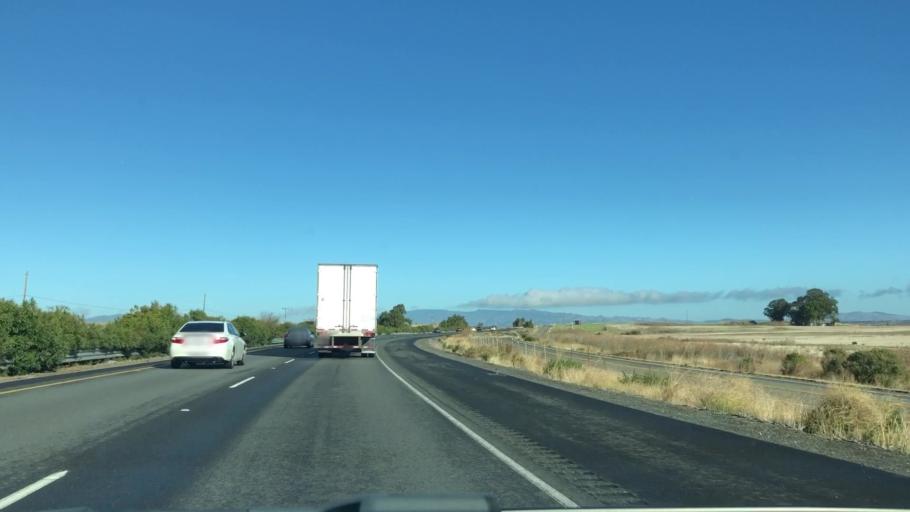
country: US
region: California
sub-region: Solano County
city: Benicia
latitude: 38.1356
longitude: -122.1101
